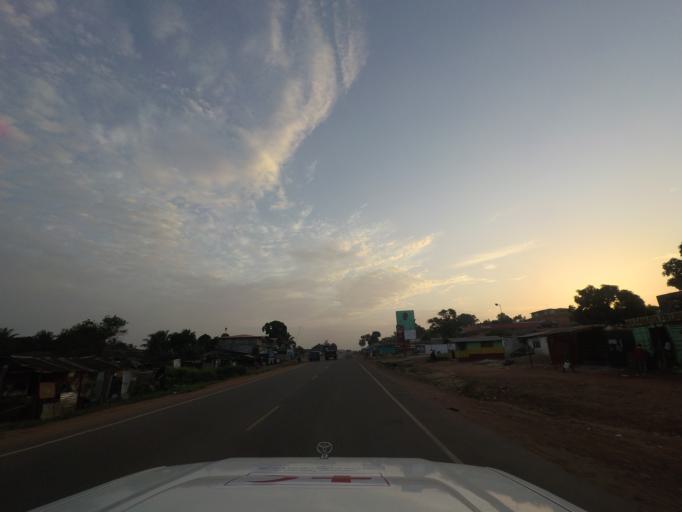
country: LR
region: Montserrado
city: Monrovia
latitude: 6.3095
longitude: -10.6705
